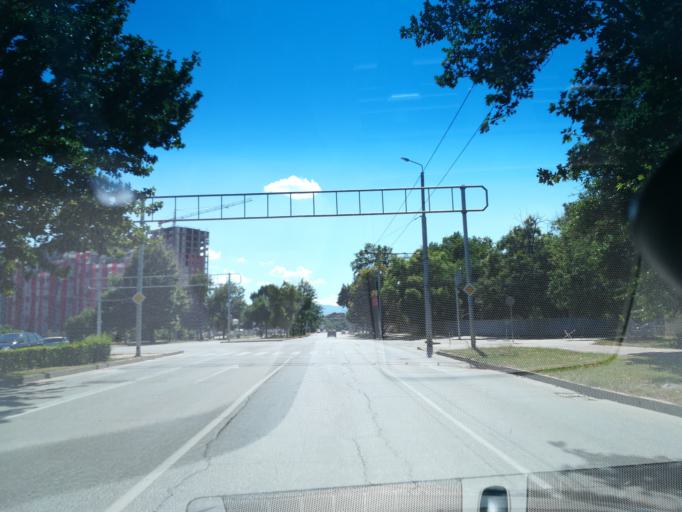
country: BG
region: Plovdiv
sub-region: Obshtina Plovdiv
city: Plovdiv
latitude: 42.1289
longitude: 24.7729
